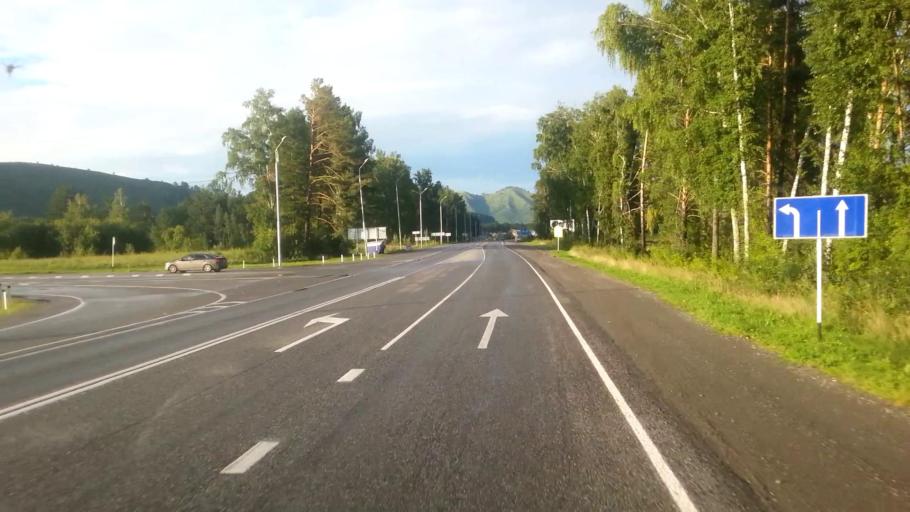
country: RU
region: Altay
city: Souzga
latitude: 51.8814
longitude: 85.8313
